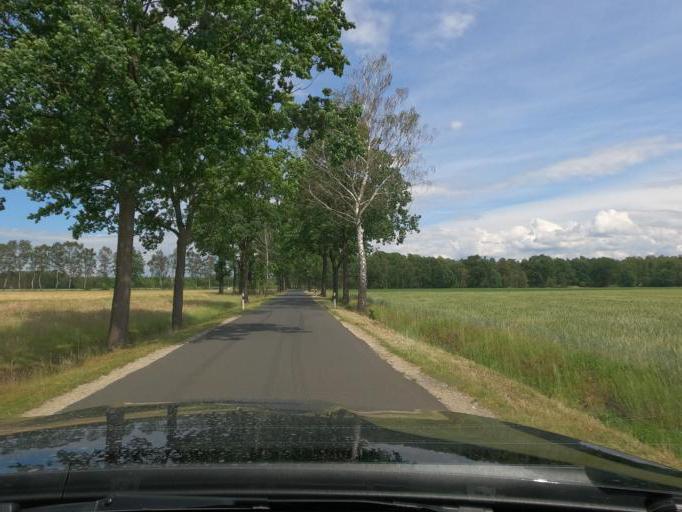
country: DE
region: Lower Saxony
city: Lindwedel
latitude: 52.6104
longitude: 9.6276
